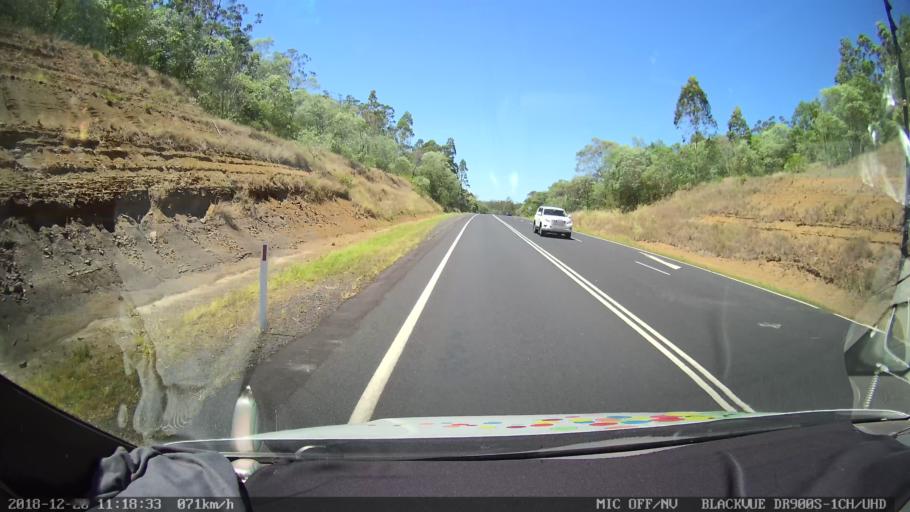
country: AU
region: New South Wales
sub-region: Richmond Valley
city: Casino
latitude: -29.0529
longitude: 153.0064
